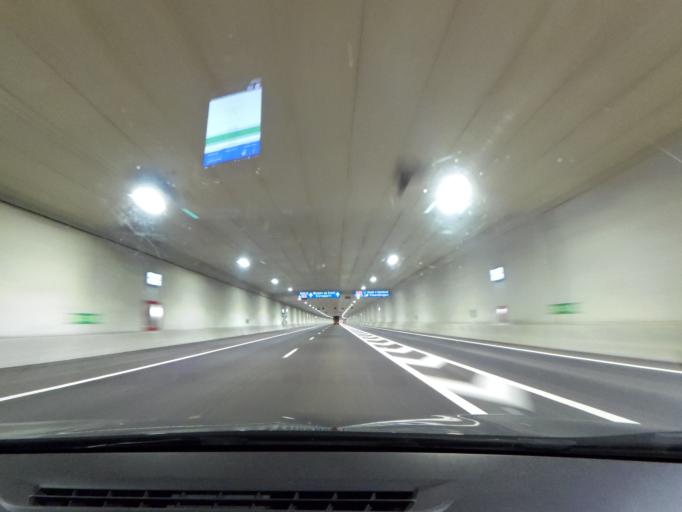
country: NL
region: South Holland
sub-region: Gemeente Vlaardingen
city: Vlaardingen
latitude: 51.9432
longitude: 4.3583
